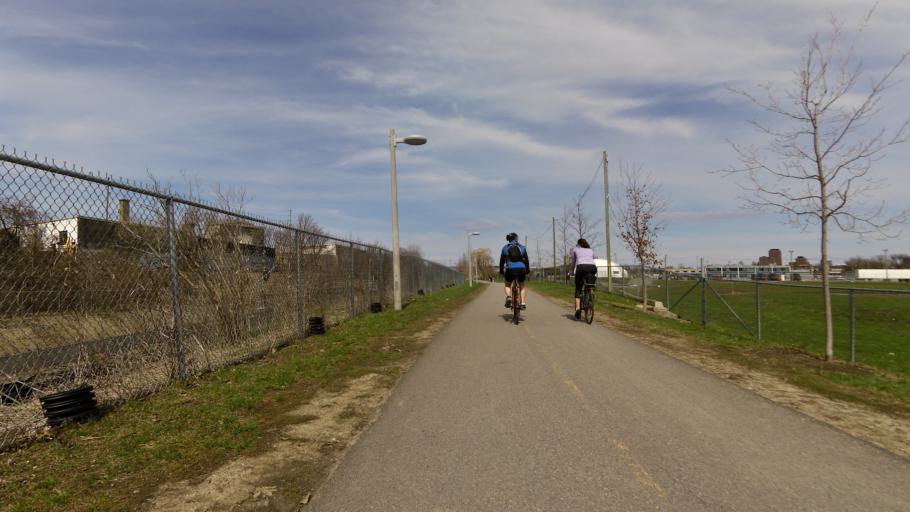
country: CA
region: Ontario
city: Ottawa
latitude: 45.4048
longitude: -75.7152
